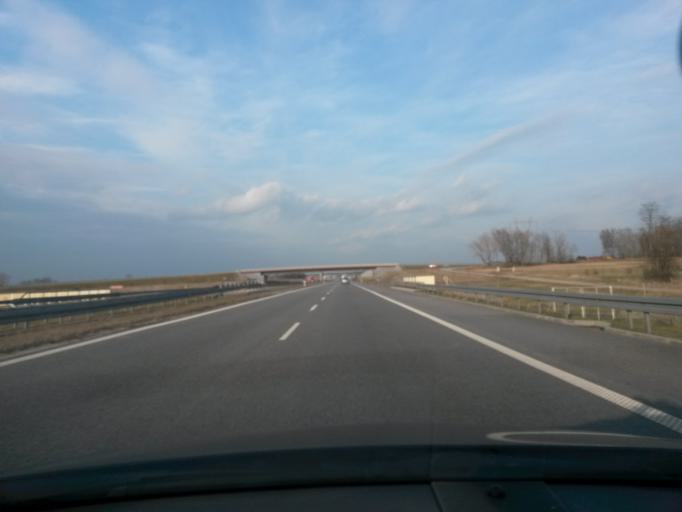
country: PL
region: Lodz Voivodeship
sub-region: Powiat brzezinski
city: Dmosin
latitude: 51.9347
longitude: 19.8073
